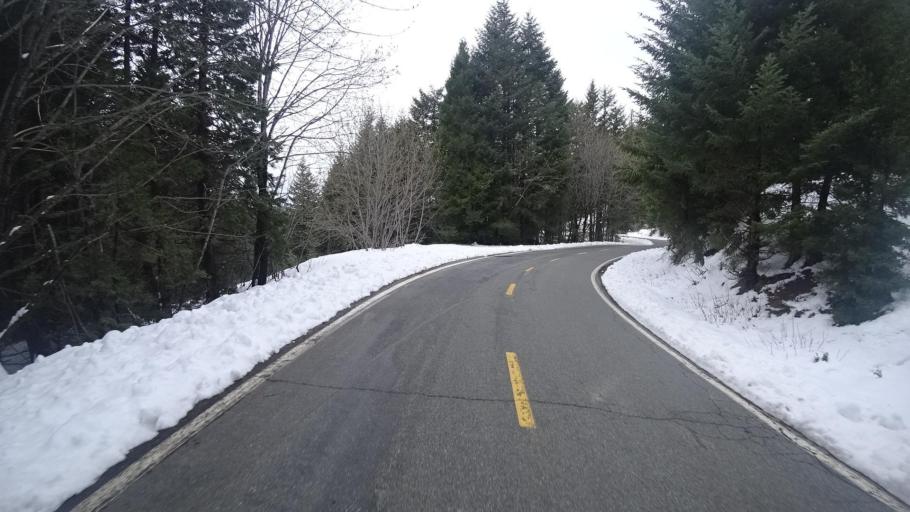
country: US
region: California
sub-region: Humboldt County
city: Willow Creek
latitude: 40.8679
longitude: -123.7456
